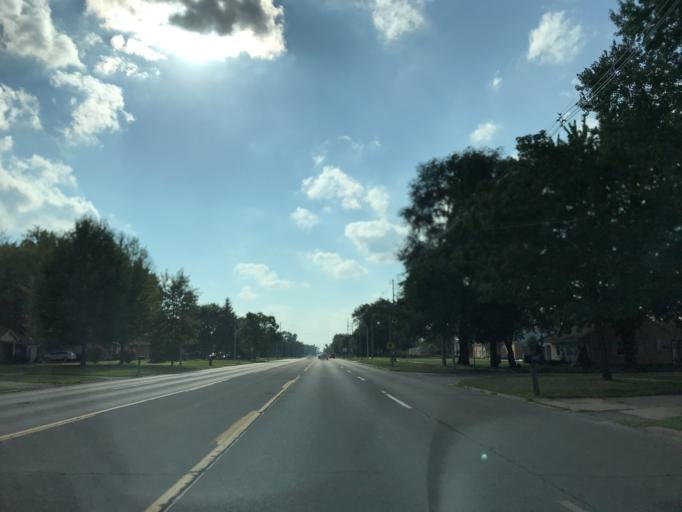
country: US
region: Michigan
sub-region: Wayne County
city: Livonia
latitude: 42.3980
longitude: -83.3407
